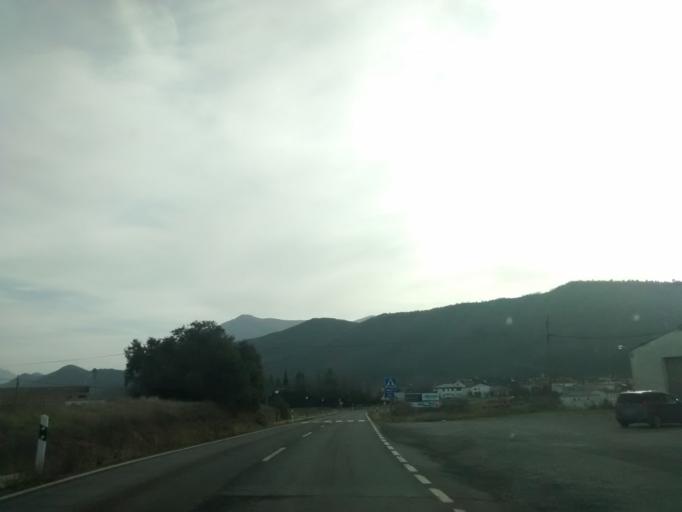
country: ES
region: Aragon
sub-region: Provincia de Huesca
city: Bailo
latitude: 42.5620
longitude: -0.7900
